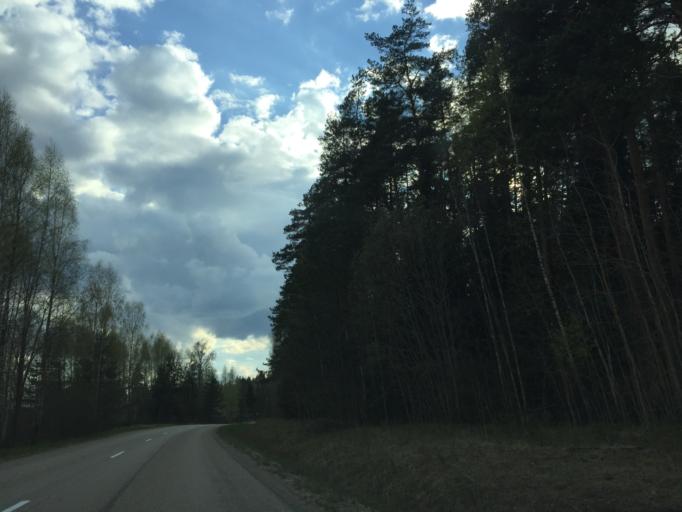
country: LV
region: Priekuli
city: Priekuli
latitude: 57.3685
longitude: 25.3967
